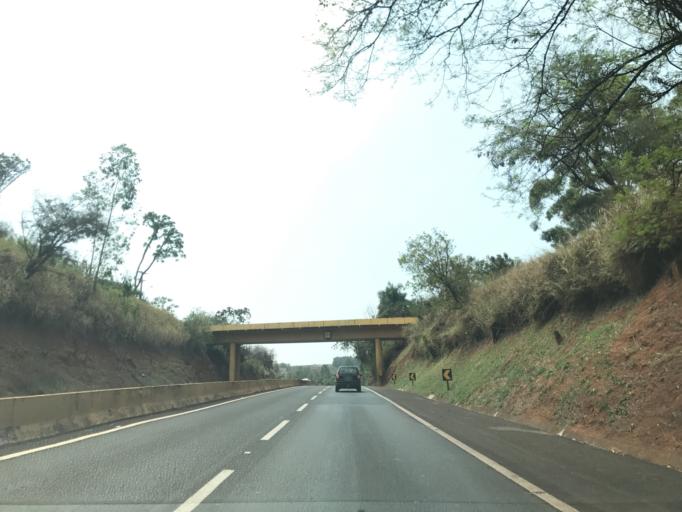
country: BR
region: Parana
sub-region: Rolandia
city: Rolandia
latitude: -23.3264
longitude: -51.3458
